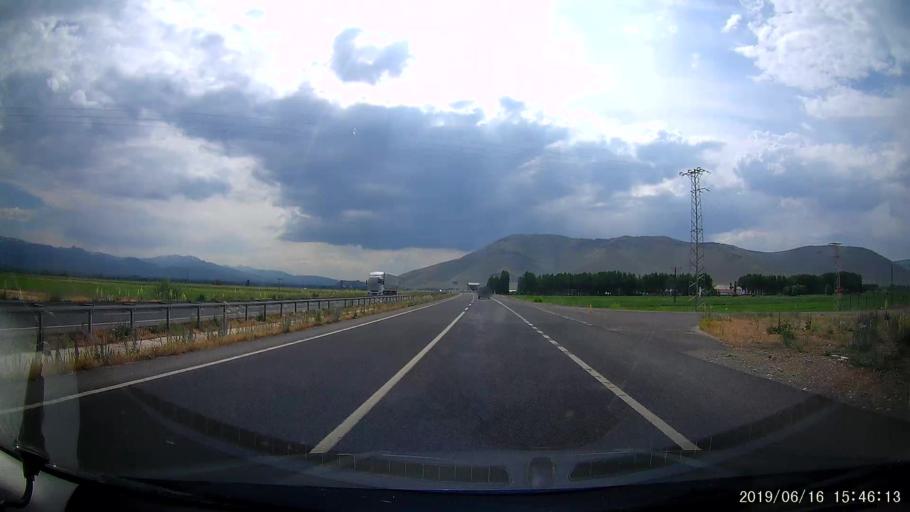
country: TR
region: Erzurum
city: Pasinler
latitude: 39.9901
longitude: 41.7490
